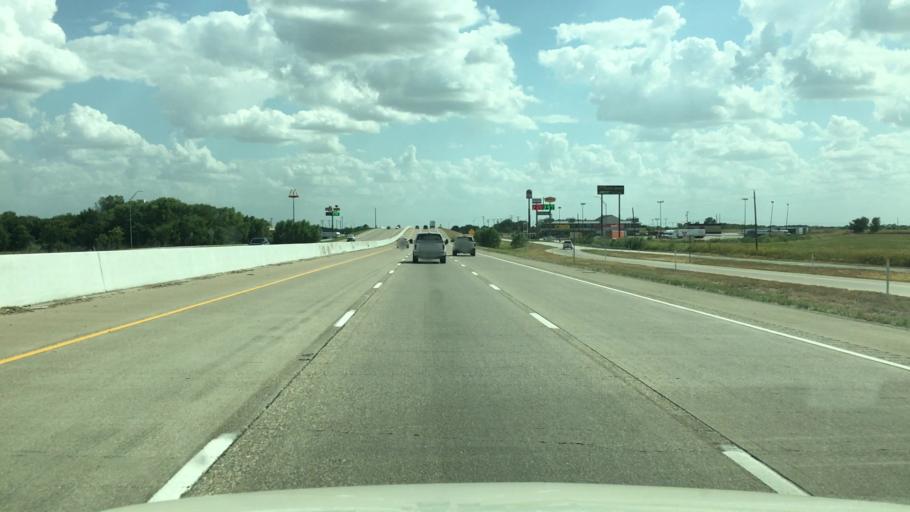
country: US
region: Texas
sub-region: Ellis County
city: Italy
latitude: 32.2009
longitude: -96.8970
